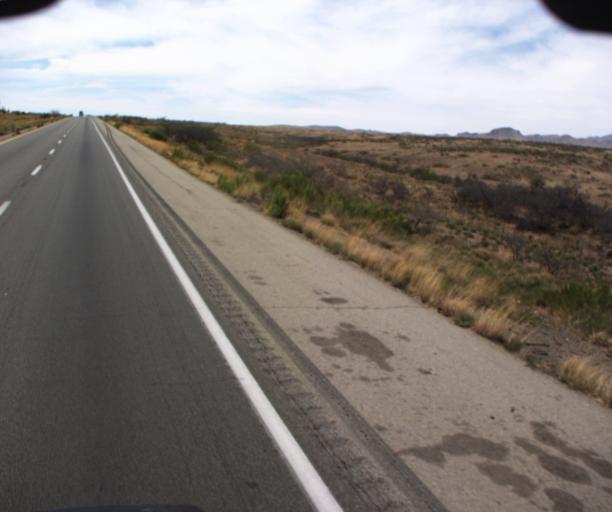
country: US
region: Arizona
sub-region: Cochise County
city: Willcox
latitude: 32.3627
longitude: -109.6431
